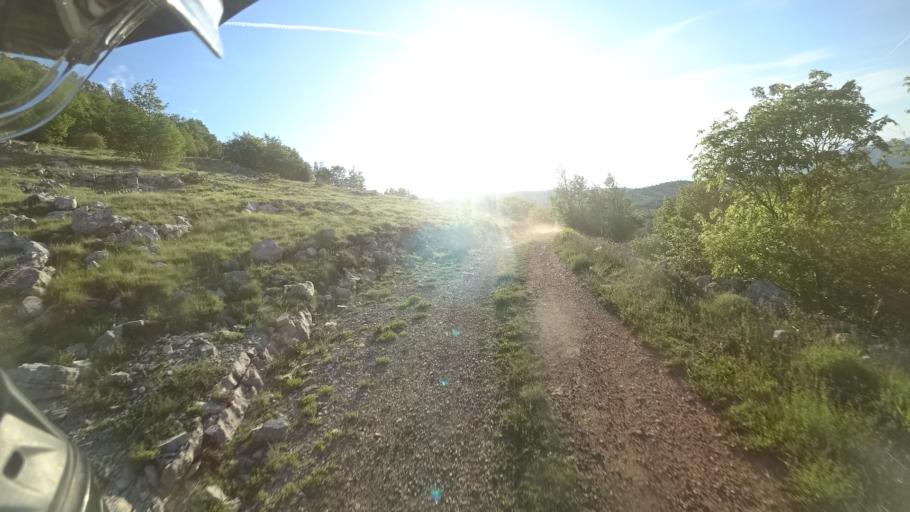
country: HR
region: Sibensko-Kniniska
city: Drnis
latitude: 43.8706
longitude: 16.3642
